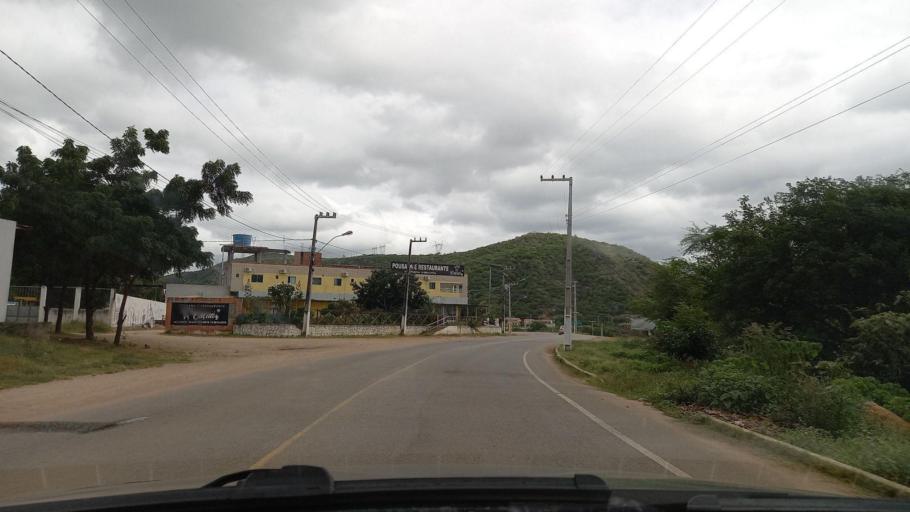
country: BR
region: Sergipe
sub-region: Caninde De Sao Francisco
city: Caninde de Sao Francisco
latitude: -9.6423
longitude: -37.7838
